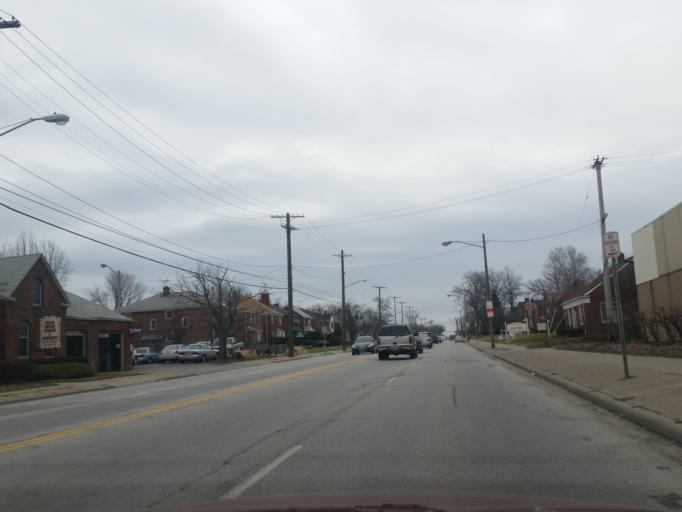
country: US
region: Ohio
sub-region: Cuyahoga County
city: University Heights
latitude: 41.5013
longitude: -81.5553
